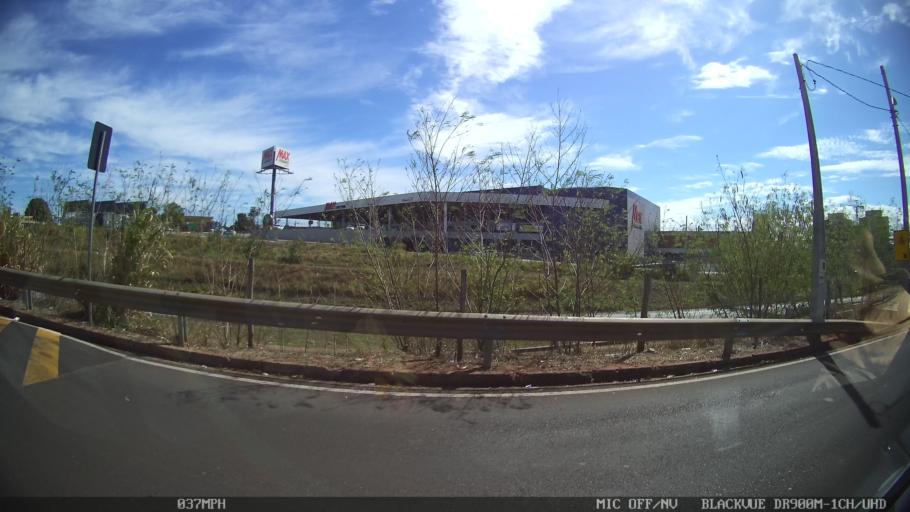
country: BR
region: Sao Paulo
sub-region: Sao Jose Do Rio Preto
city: Sao Jose do Rio Preto
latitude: -20.8405
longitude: -49.3674
